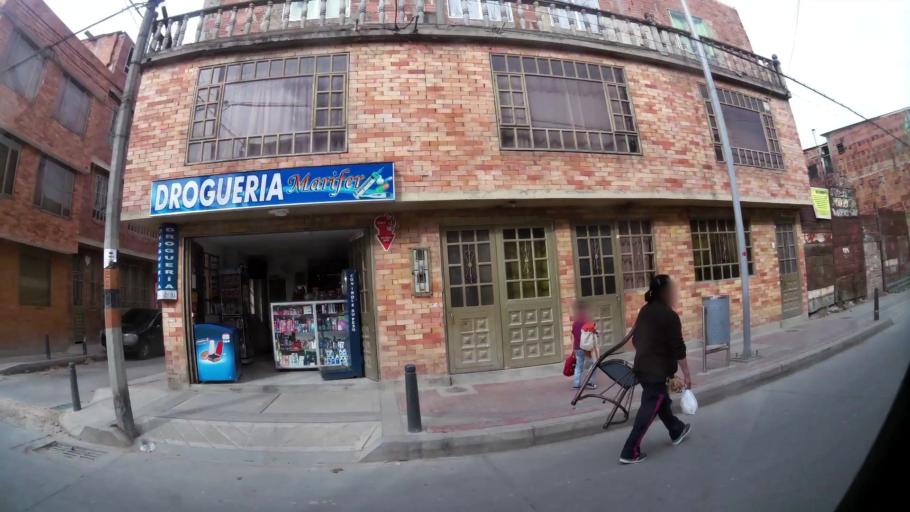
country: CO
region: Cundinamarca
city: Funza
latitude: 4.7049
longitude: -74.2102
